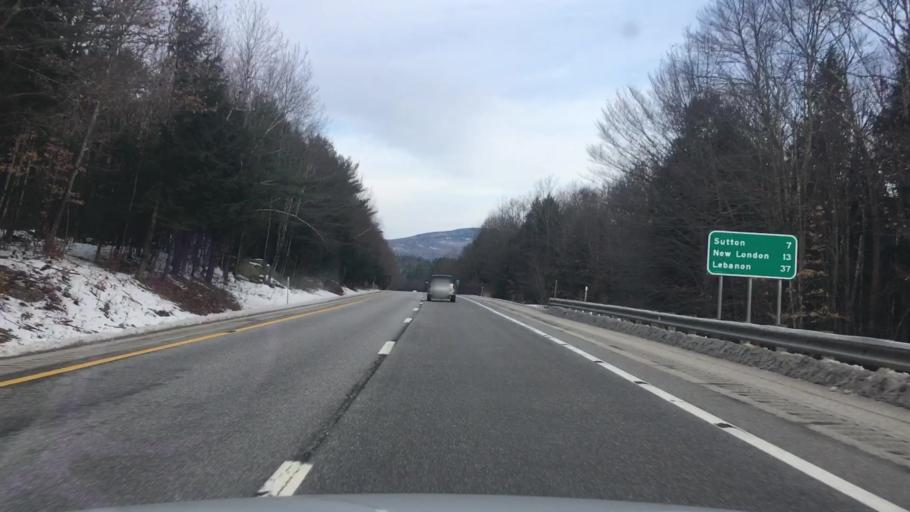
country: US
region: New Hampshire
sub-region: Merrimack County
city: Sutton
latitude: 43.3017
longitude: -71.8408
